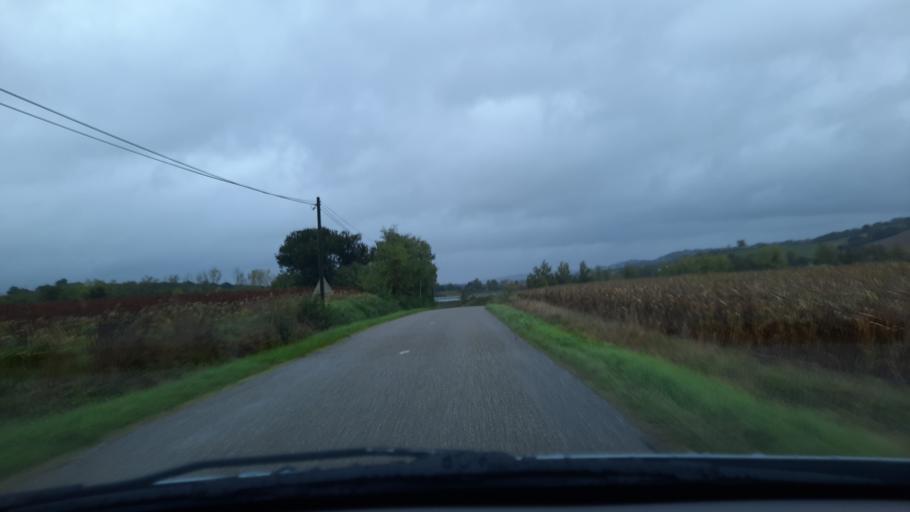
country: FR
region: Midi-Pyrenees
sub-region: Departement du Tarn-et-Garonne
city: Lafrancaise
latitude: 44.1791
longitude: 1.2699
